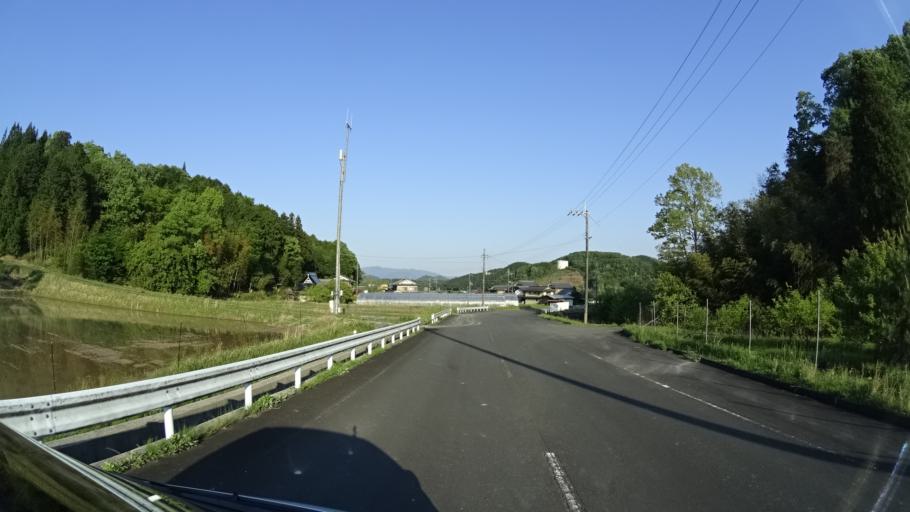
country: JP
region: Kyoto
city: Kameoka
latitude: 35.1090
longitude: 135.4410
